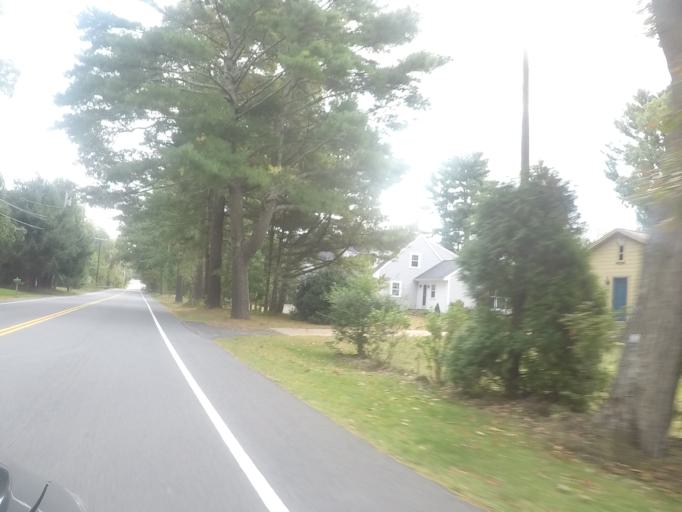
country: US
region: Massachusetts
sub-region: Bristol County
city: Smith Mills
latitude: 41.6816
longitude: -71.0151
